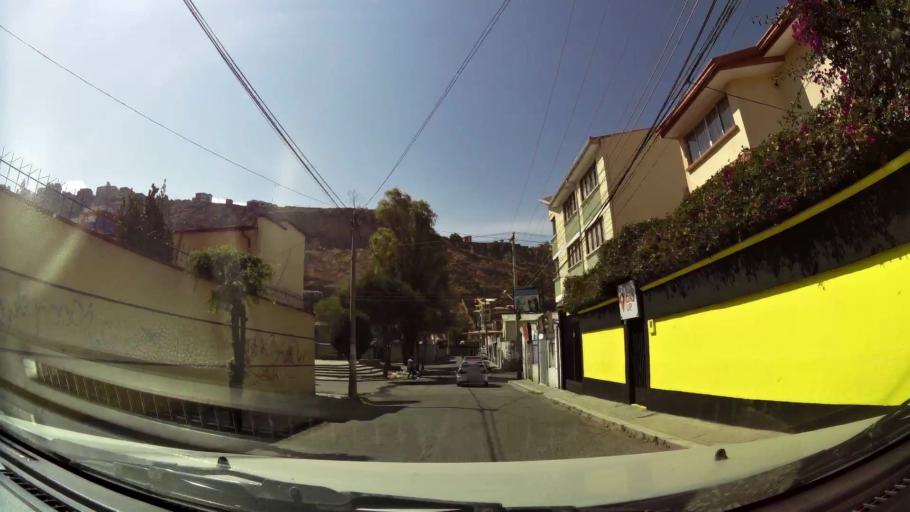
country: BO
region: La Paz
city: La Paz
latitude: -16.5208
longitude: -68.0868
